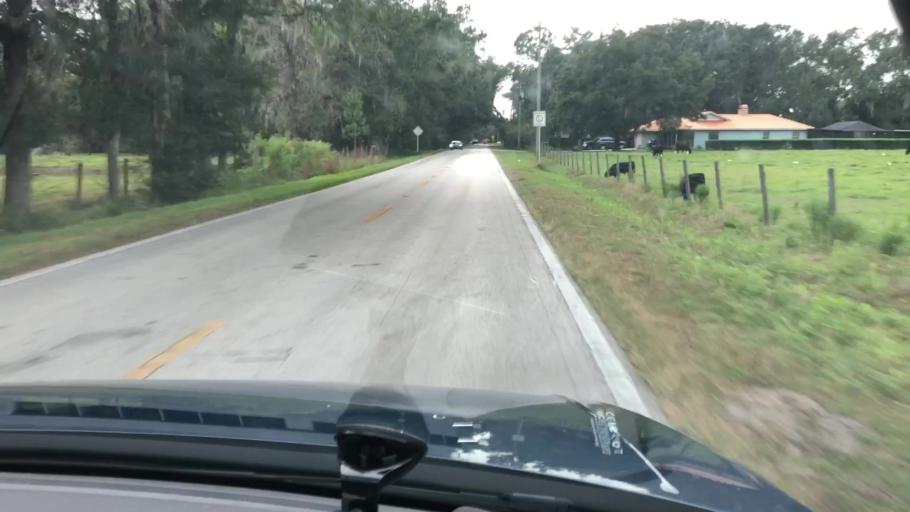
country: US
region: Florida
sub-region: Polk County
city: Kathleen
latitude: 28.1243
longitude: -82.0357
